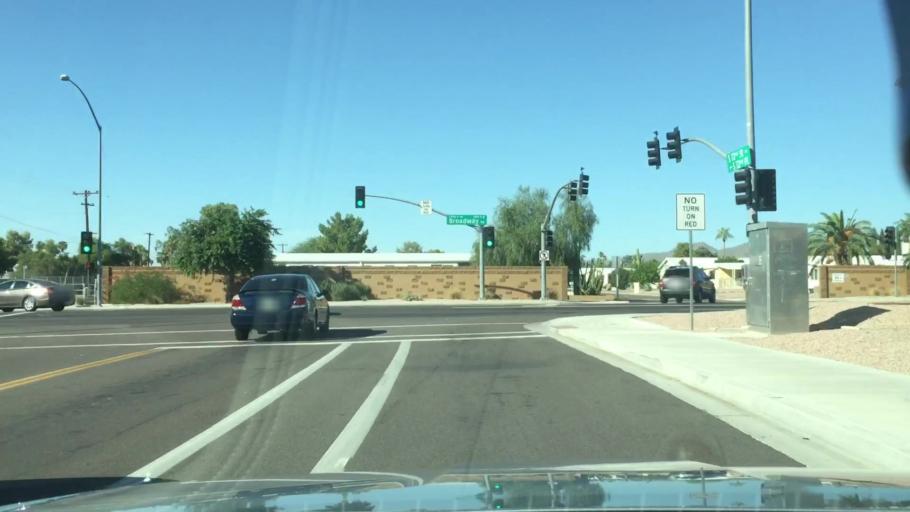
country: US
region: Arizona
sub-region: Maricopa County
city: Gilbert
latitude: 33.4076
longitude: -111.6759
